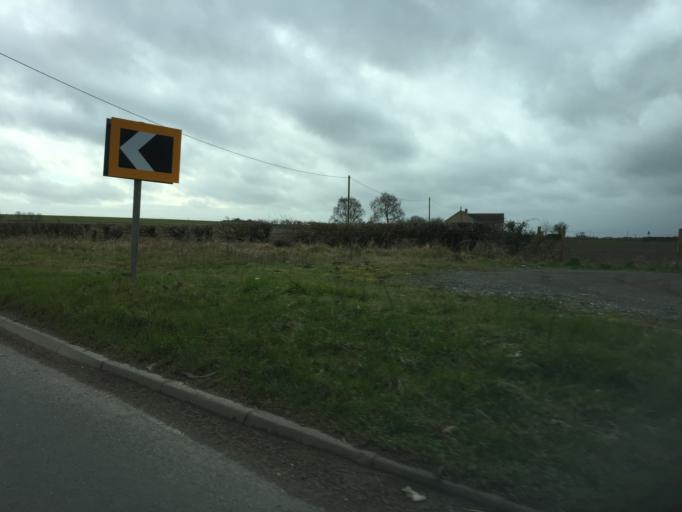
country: GB
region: England
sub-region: Gloucestershire
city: Lechlade
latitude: 51.6790
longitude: -1.6755
